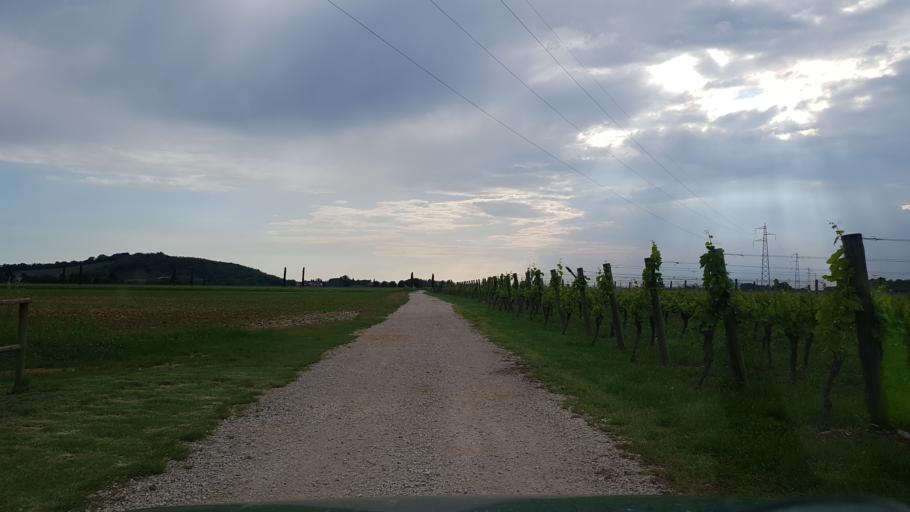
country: IT
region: Friuli Venezia Giulia
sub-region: Provincia di Gorizia
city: San Lorenzo Isontino
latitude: 45.9198
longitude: 13.5395
